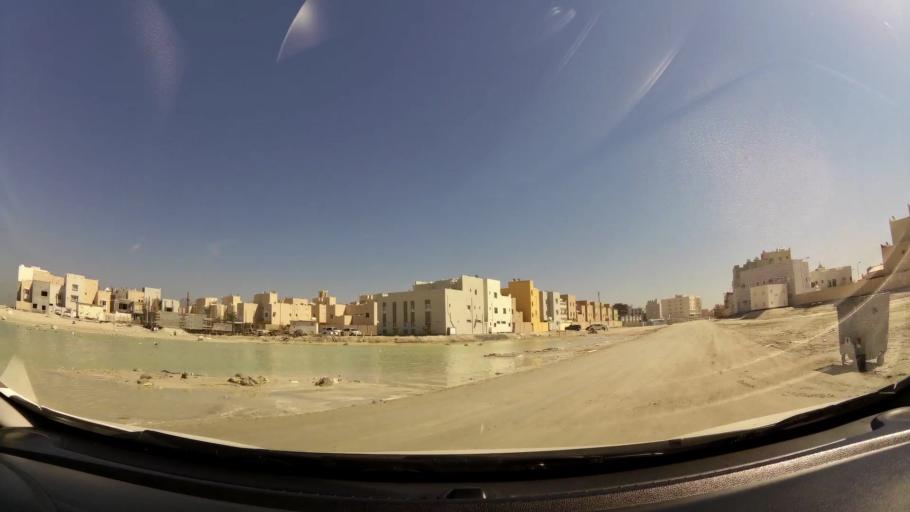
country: BH
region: Muharraq
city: Al Muharraq
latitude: 26.2728
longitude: 50.5953
